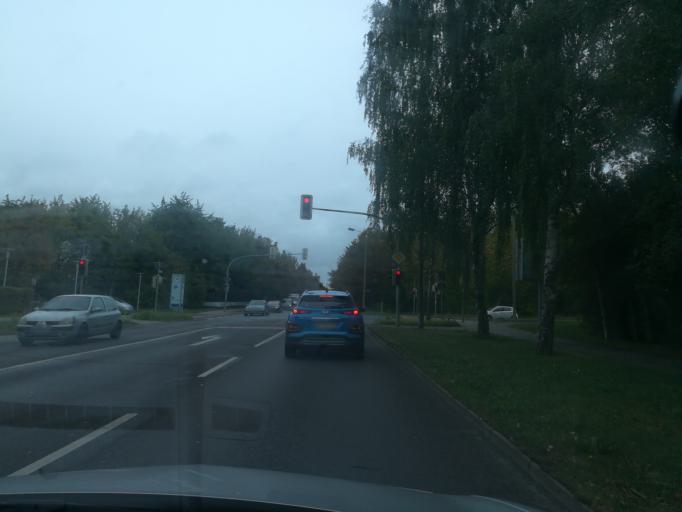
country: DE
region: Saxony-Anhalt
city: Ebendorf
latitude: 52.1564
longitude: 11.5837
